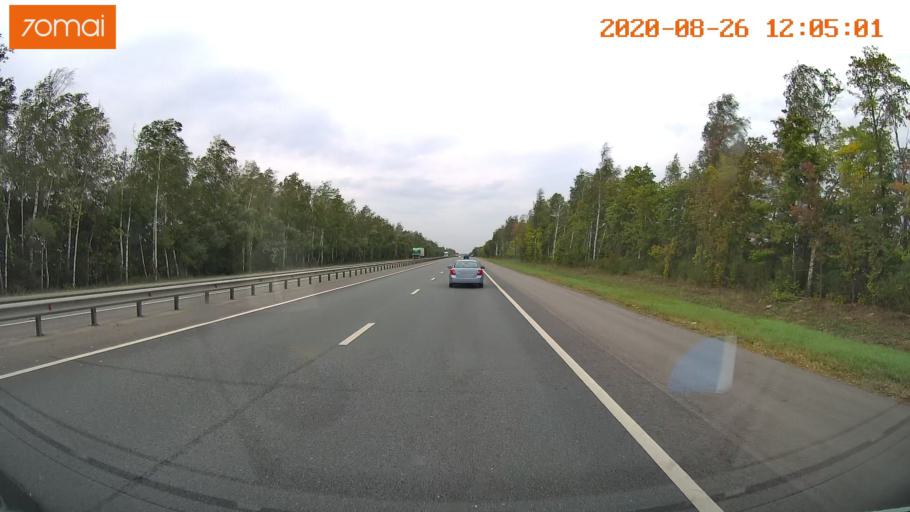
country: RU
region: Rjazan
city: Kiritsy
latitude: 54.3164
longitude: 40.1768
